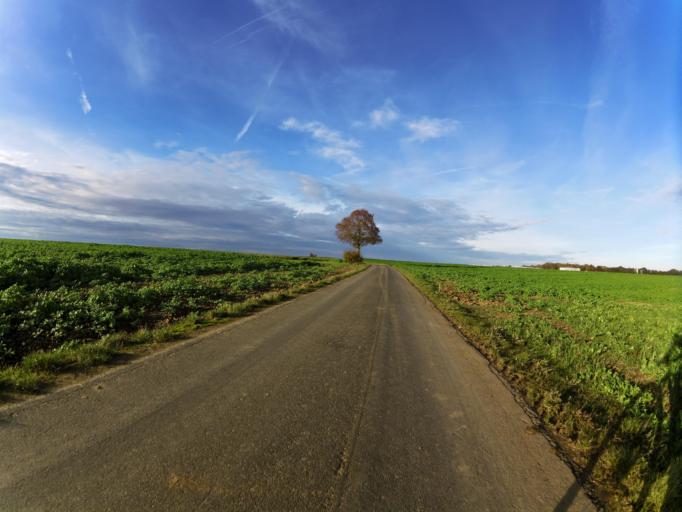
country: DE
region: Bavaria
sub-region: Regierungsbezirk Unterfranken
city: Giebelstadt
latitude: 49.6809
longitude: 9.9399
